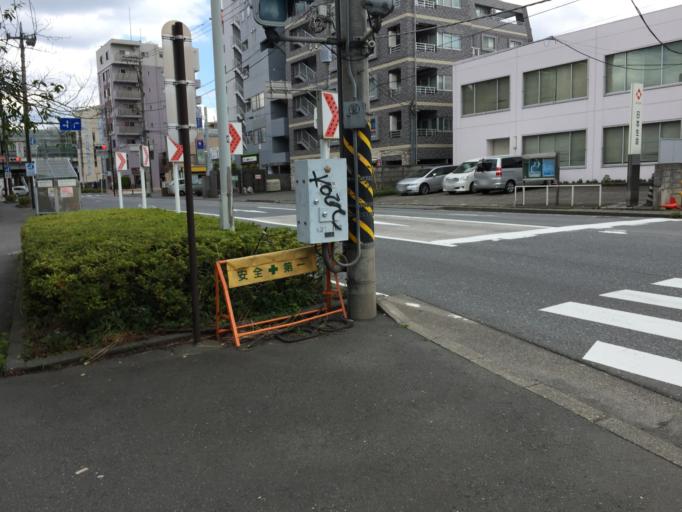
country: JP
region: Tokyo
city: Chofugaoka
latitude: 35.6220
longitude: 139.5679
